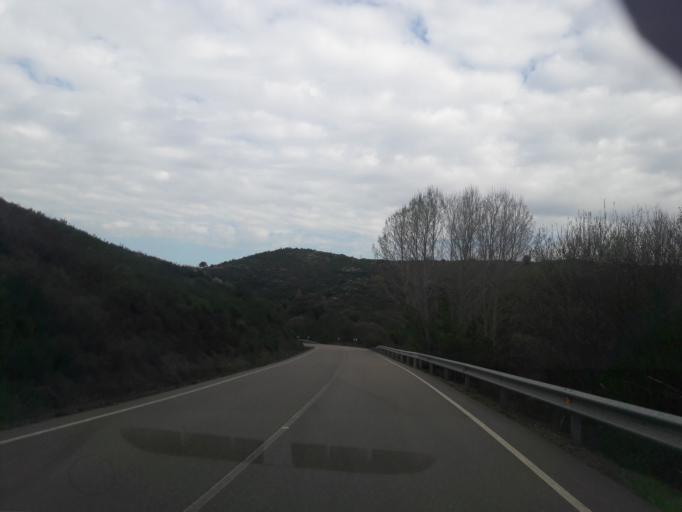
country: ES
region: Castille and Leon
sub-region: Provincia de Salamanca
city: Serradilla del Arroyo
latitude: 40.5137
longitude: -6.3615
